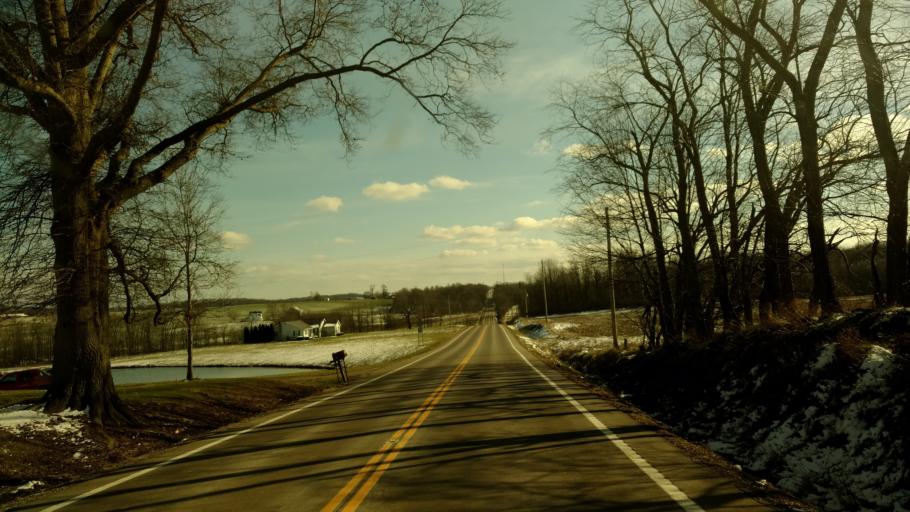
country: US
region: Ohio
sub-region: Ashland County
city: Ashland
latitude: 40.7661
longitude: -82.2597
